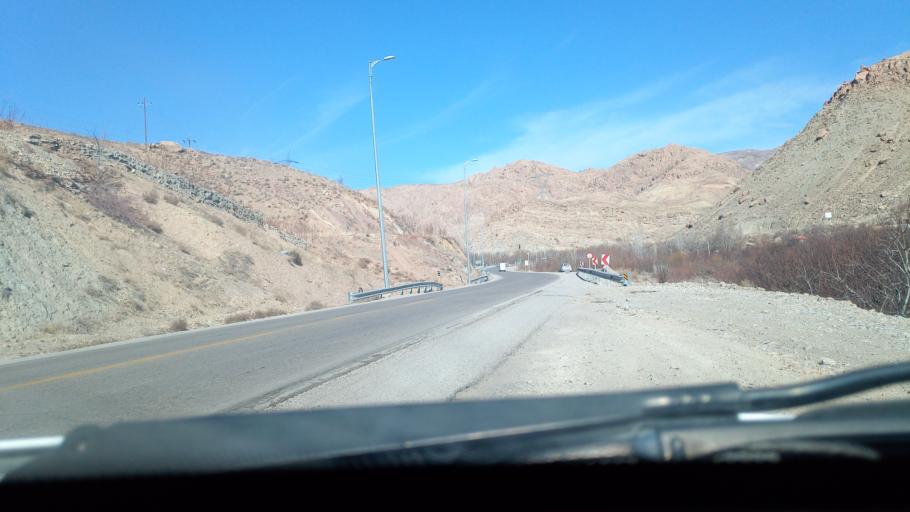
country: IR
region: Khorasan-e Shomali
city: Esfarayen
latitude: 37.1876
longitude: 57.4125
